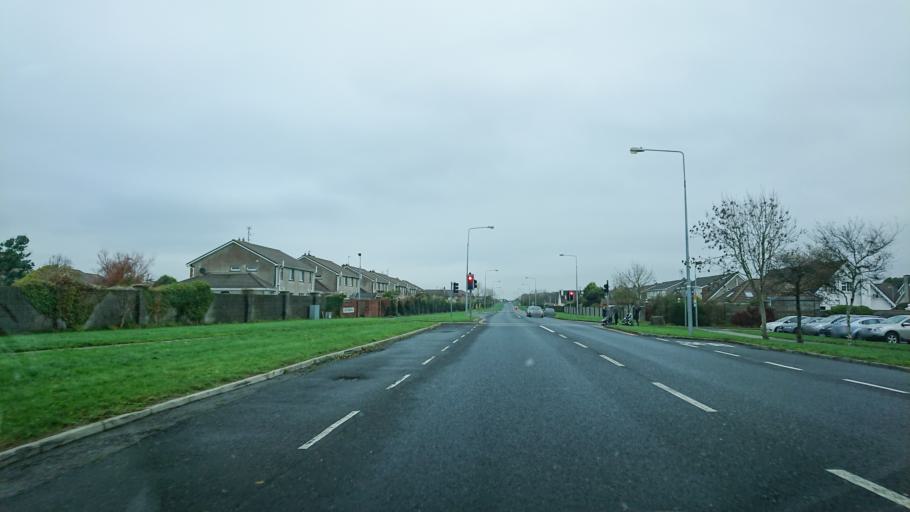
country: IE
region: Munster
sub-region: Waterford
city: Tra Mhor
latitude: 52.1608
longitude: -7.1678
